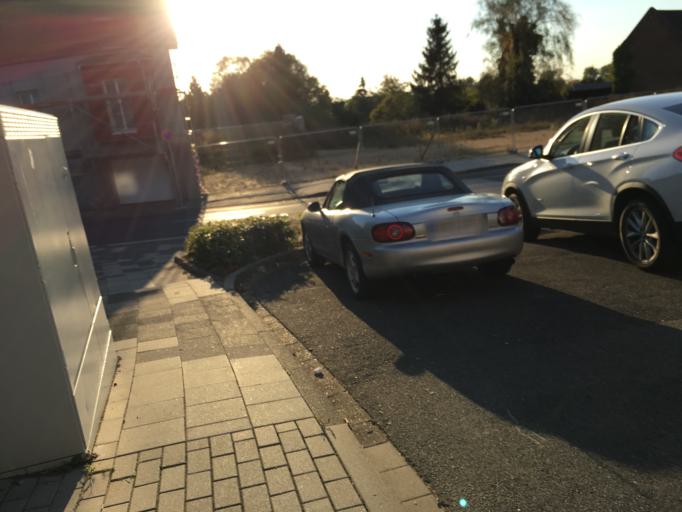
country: DE
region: North Rhine-Westphalia
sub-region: Regierungsbezirk Koln
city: Merzenich
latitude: 50.8311
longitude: 6.5259
